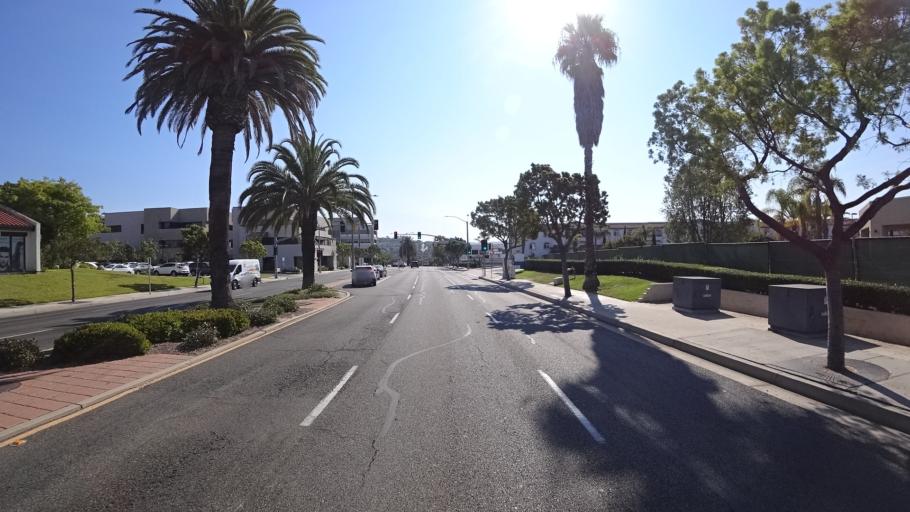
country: US
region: California
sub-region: Orange County
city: San Juan Capistrano
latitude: 33.4574
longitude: -117.6493
